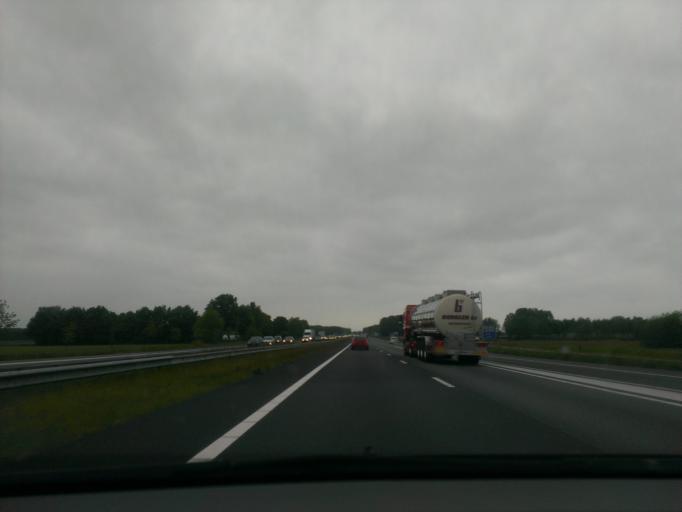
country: NL
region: Drenthe
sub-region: Gemeente De Wolden
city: Ruinen
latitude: 52.6853
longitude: 6.3839
